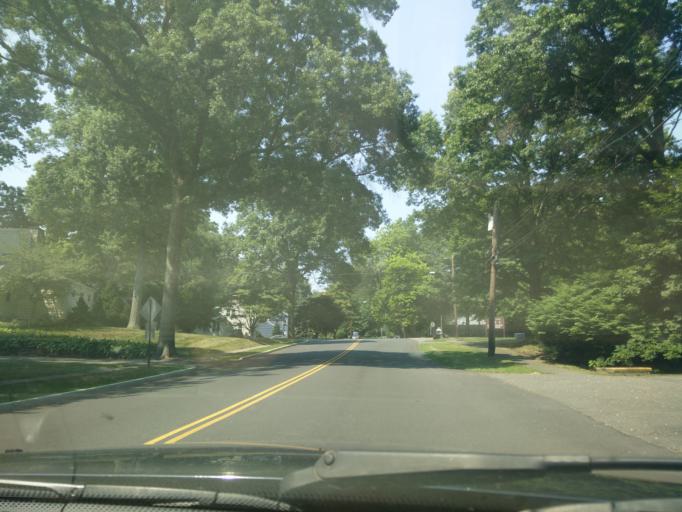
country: US
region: Connecticut
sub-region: Fairfield County
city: Fairfield
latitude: 41.1631
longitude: -73.2426
